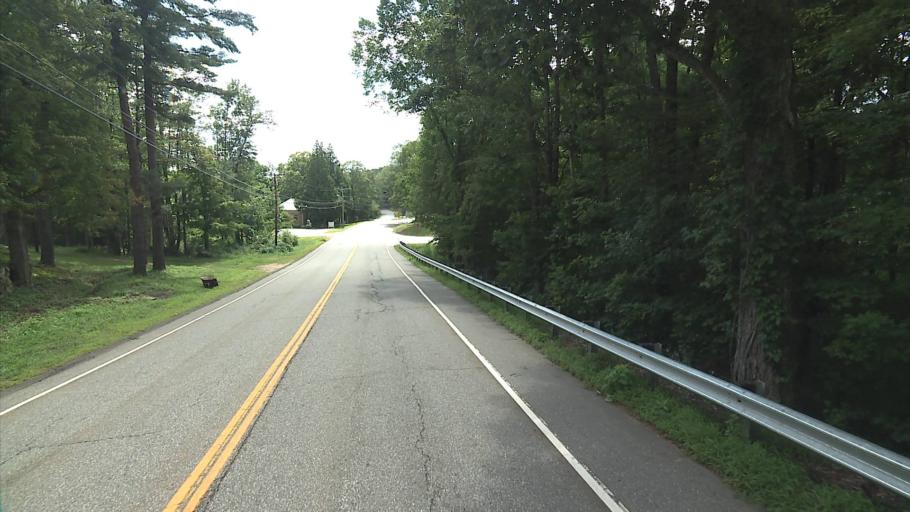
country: US
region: Massachusetts
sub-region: Hampden County
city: Holland
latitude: 41.9917
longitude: -72.1576
